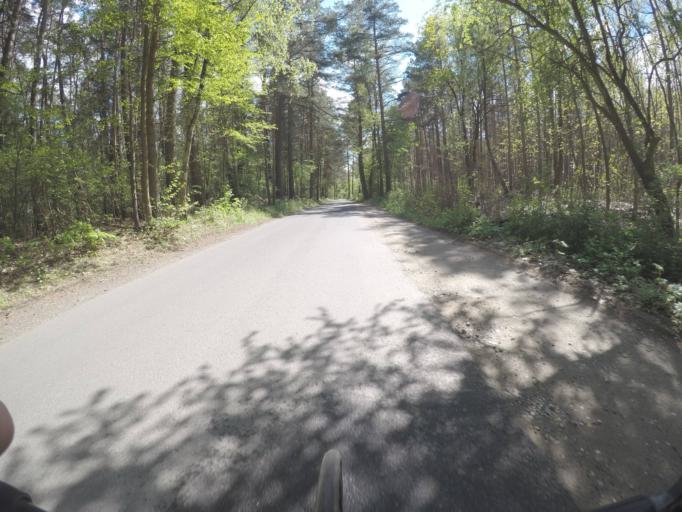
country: DE
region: Brandenburg
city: Bernau bei Berlin
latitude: 52.7115
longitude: 13.5909
